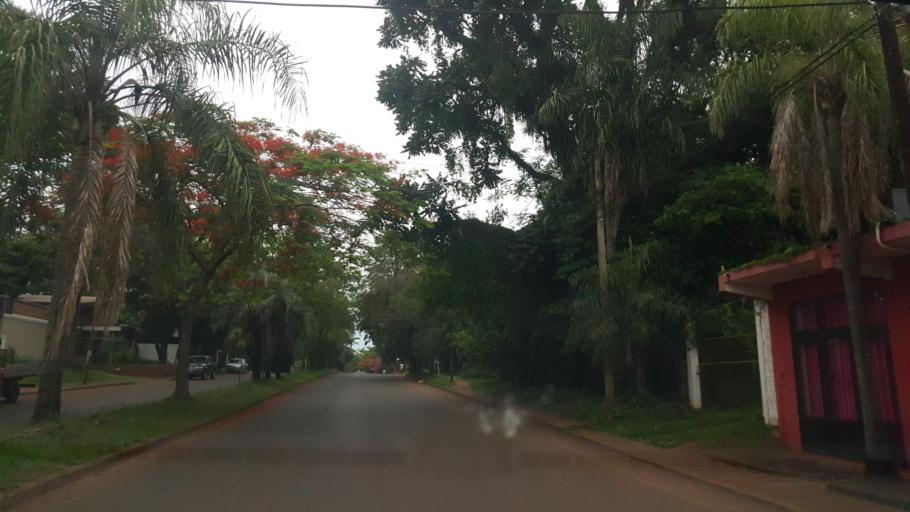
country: AR
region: Misiones
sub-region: Departamento de Capital
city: Posadas
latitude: -27.3607
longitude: -55.9308
